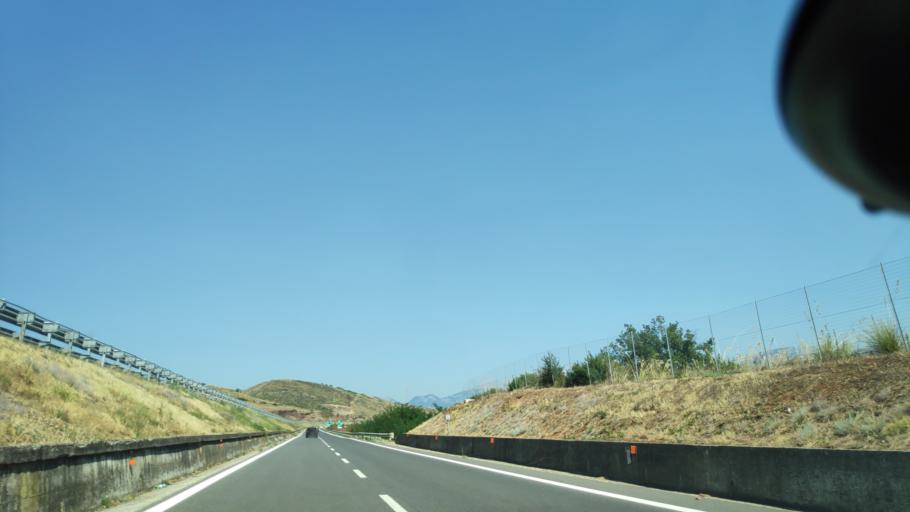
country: IT
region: Calabria
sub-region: Provincia di Cosenza
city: Firmo
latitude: 39.7403
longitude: 16.2301
